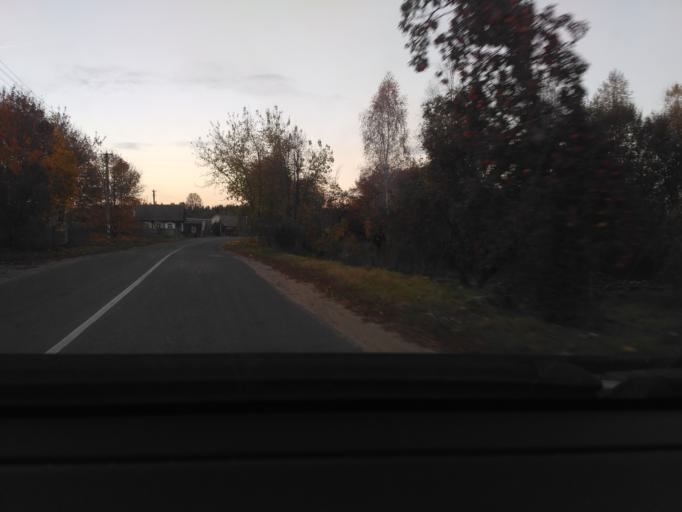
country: BY
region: Minsk
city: Loshnitsa
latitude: 54.3633
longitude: 28.6247
